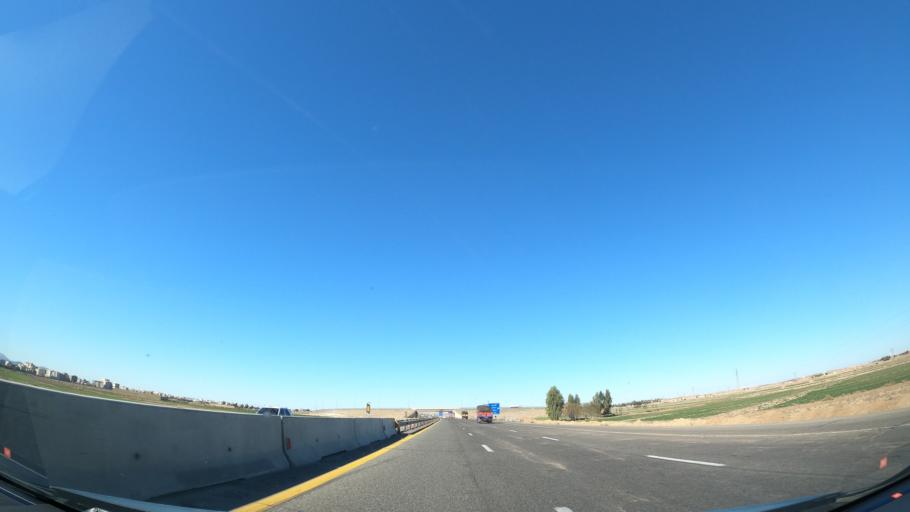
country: IR
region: Qom
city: Qom
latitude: 34.6454
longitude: 50.9378
